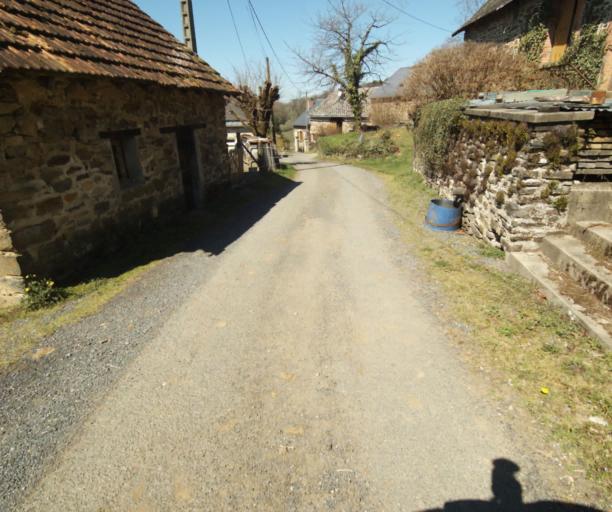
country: FR
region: Limousin
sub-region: Departement de la Correze
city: Saint-Clement
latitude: 45.3410
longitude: 1.7063
